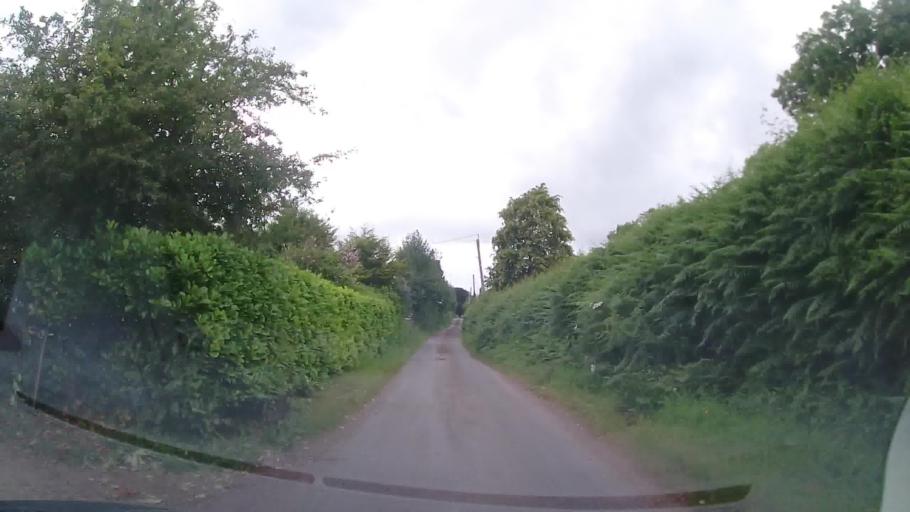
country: GB
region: England
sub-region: Shropshire
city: Prees
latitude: 52.9186
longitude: -2.6886
